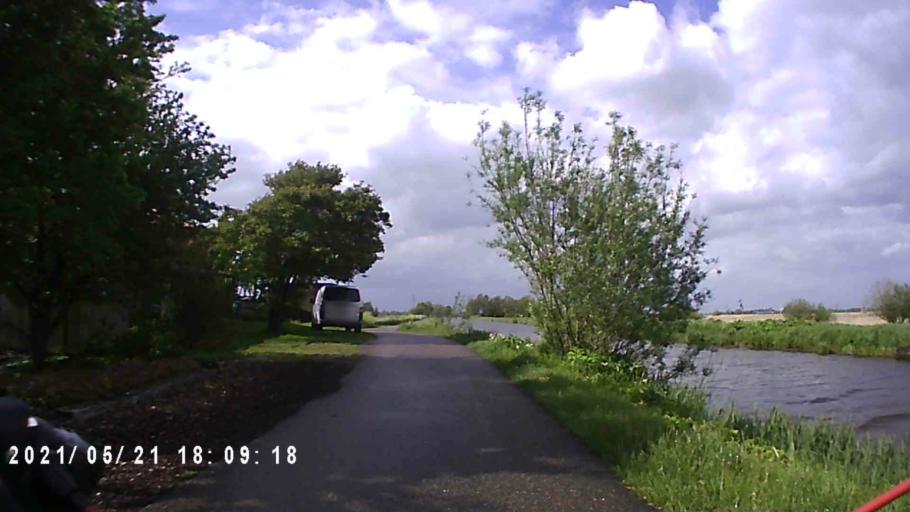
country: NL
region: Groningen
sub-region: Gemeente Zuidhorn
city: Zuidhorn
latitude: 53.1985
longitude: 6.4142
